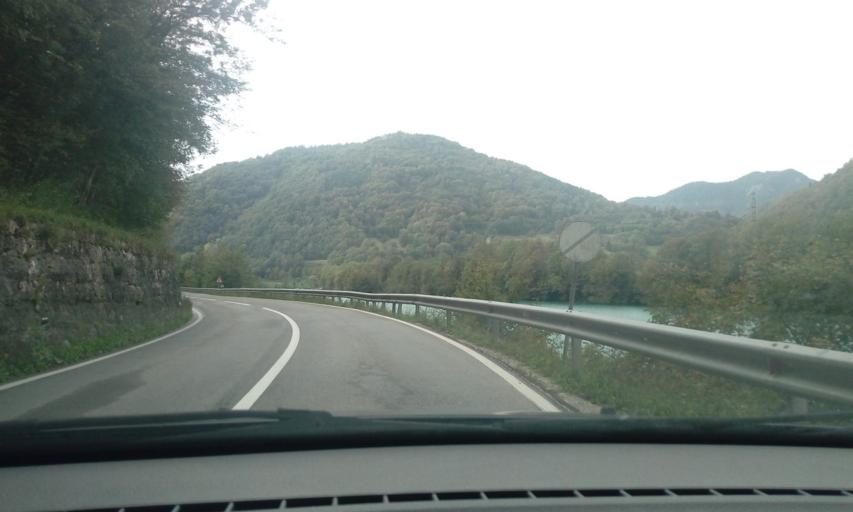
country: SI
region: Tolmin
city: Tolmin
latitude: 46.1628
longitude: 13.7516
